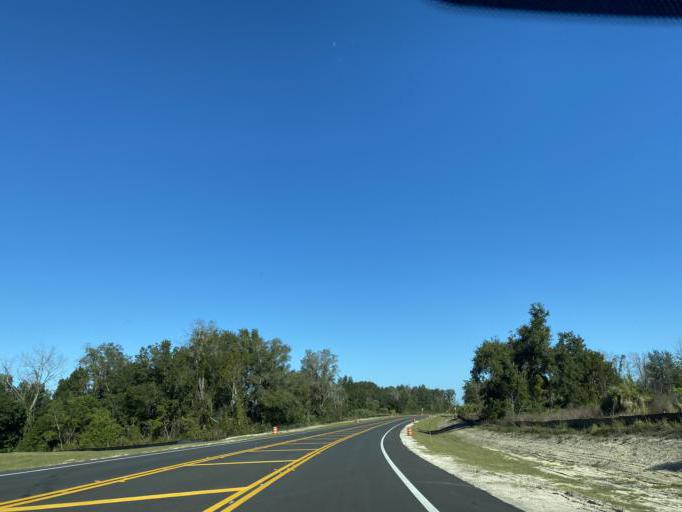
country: US
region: Florida
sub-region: Lake County
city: Mount Plymouth
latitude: 28.8171
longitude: -81.5221
